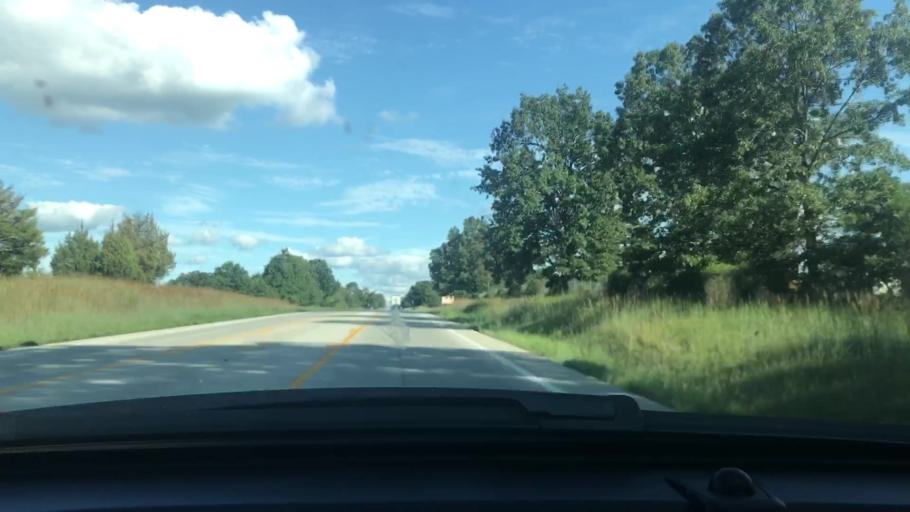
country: US
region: Missouri
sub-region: Howell County
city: West Plains
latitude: 36.6540
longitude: -91.6951
